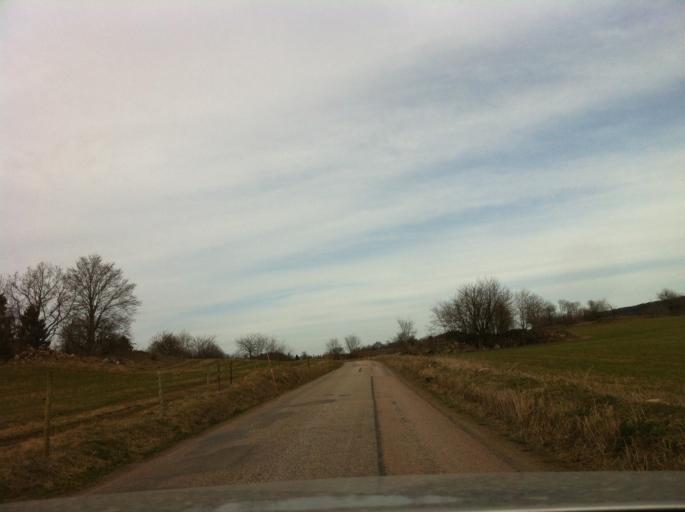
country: SE
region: Vaestra Goetaland
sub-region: Skara Kommun
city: Axvall
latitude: 58.4079
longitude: 13.6663
